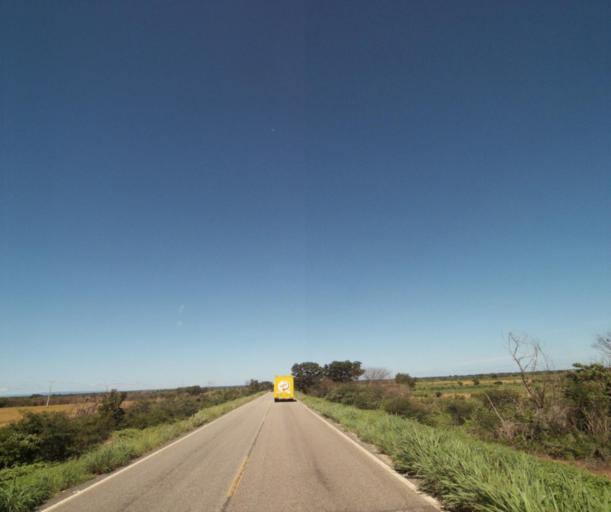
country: BR
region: Bahia
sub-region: Palmas De Monte Alto
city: Palmas de Monte Alto
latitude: -14.2574
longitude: -43.2603
